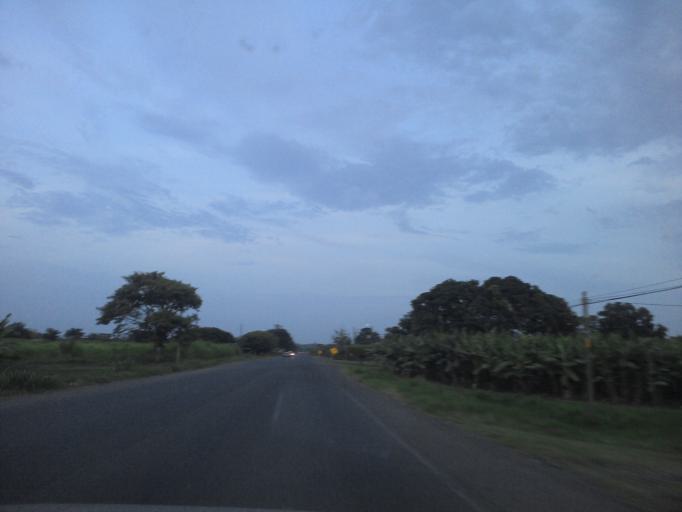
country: MX
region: Veracruz
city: San Rafael
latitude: 20.1914
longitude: -96.8461
